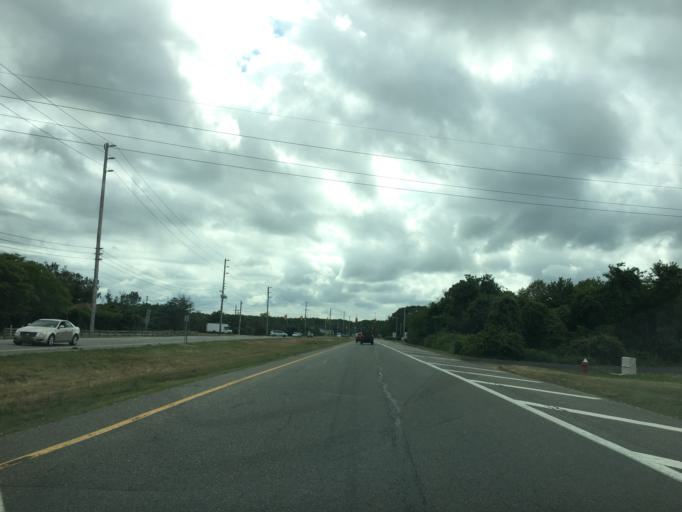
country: US
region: New York
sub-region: Suffolk County
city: Mattituck
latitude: 40.9887
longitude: -72.5495
